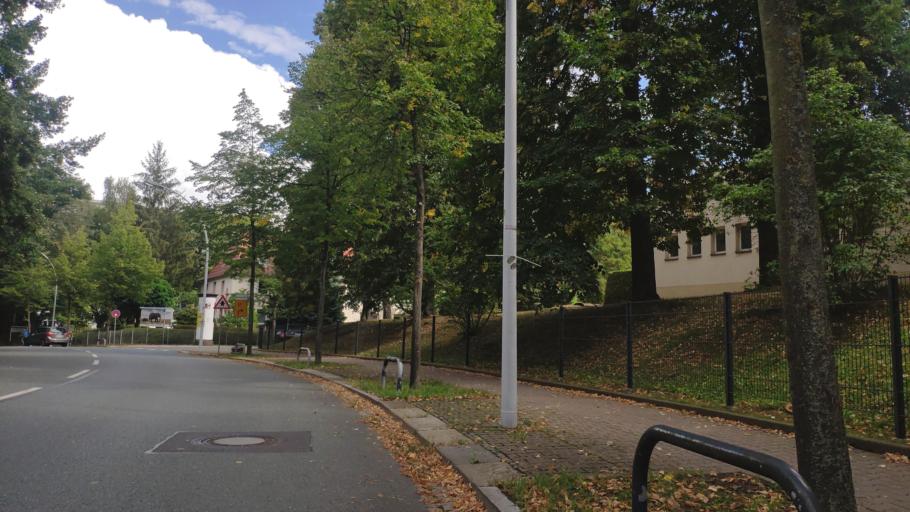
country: DE
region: Saxony
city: Chemnitz
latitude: 50.8215
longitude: 12.9073
